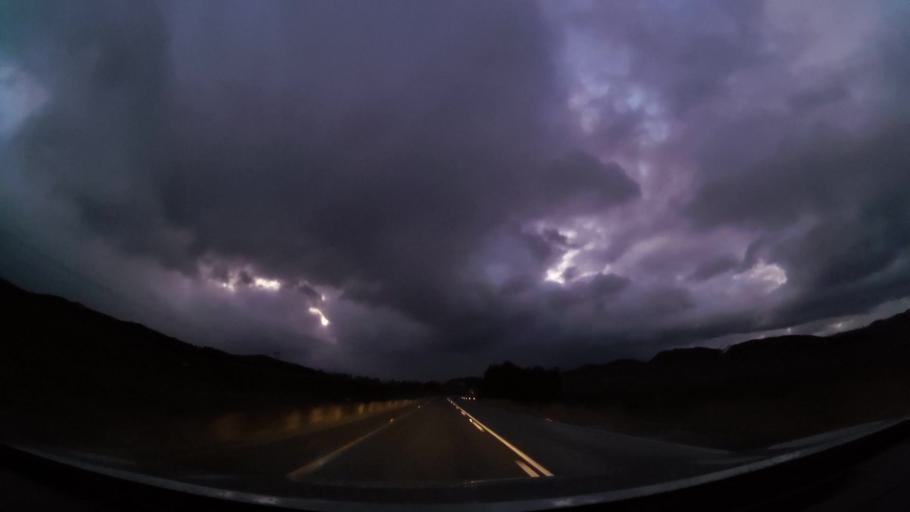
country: ZA
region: Western Cape
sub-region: Overberg District Municipality
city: Swellendam
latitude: -33.9039
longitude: 20.3956
